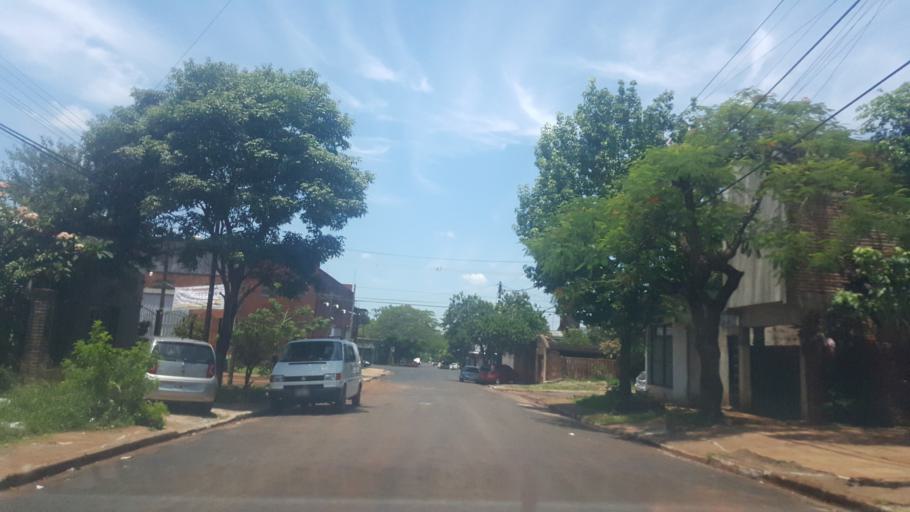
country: AR
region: Misiones
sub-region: Departamento de Capital
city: Posadas
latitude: -27.3881
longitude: -55.9091
